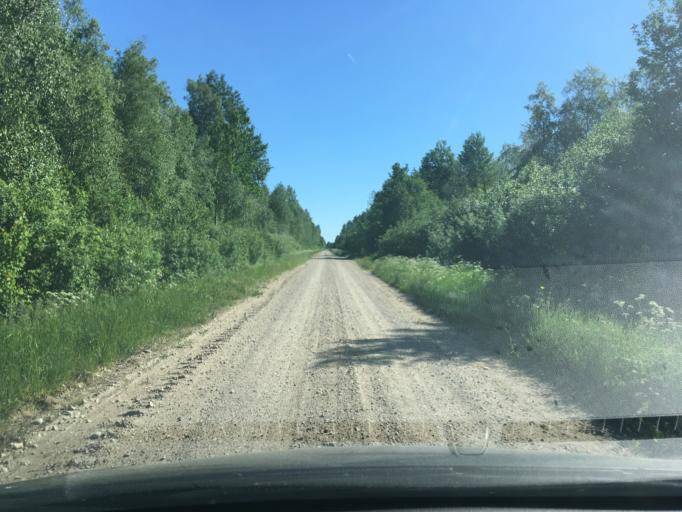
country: EE
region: Laeaene
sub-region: Lihula vald
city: Lihula
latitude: 58.6383
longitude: 23.7604
